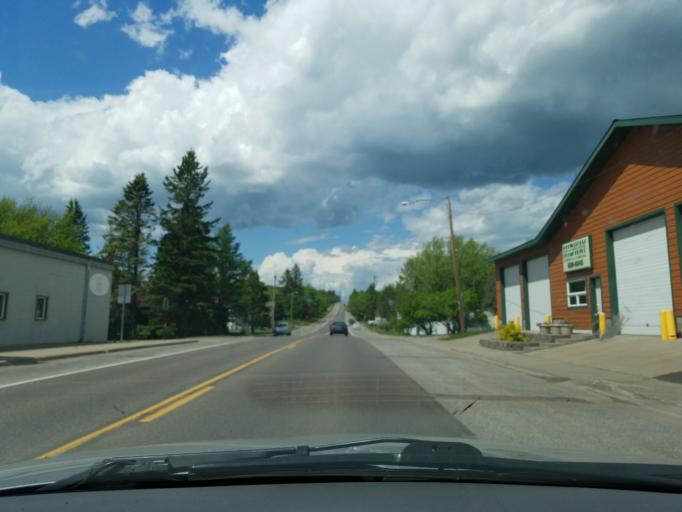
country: US
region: Minnesota
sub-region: Saint Louis County
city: Proctor
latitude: 46.7475
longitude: -92.2223
